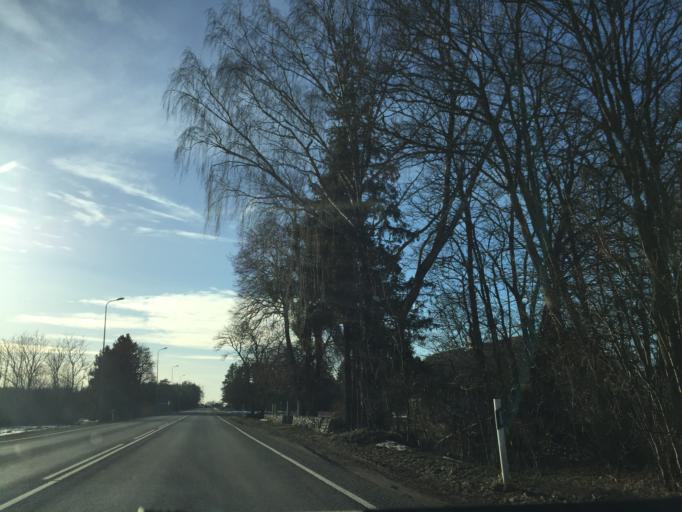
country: EE
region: Saare
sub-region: Orissaare vald
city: Orissaare
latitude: 58.5224
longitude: 22.9027
